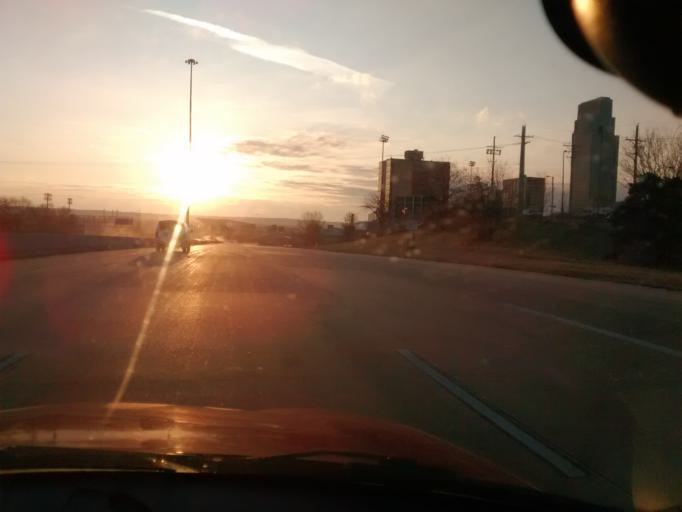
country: US
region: Nebraska
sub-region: Douglas County
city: Omaha
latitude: 41.2632
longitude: -95.9460
